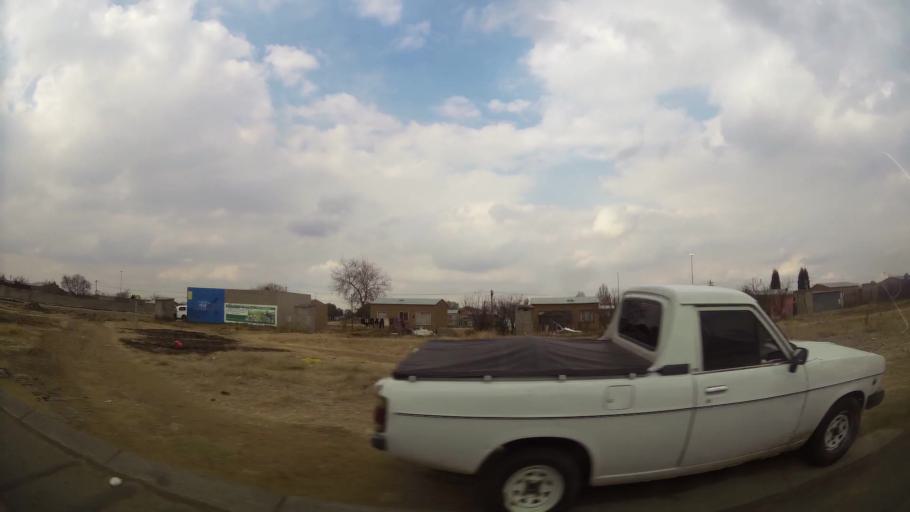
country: ZA
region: Orange Free State
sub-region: Fezile Dabi District Municipality
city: Sasolburg
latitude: -26.8506
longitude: 27.8746
